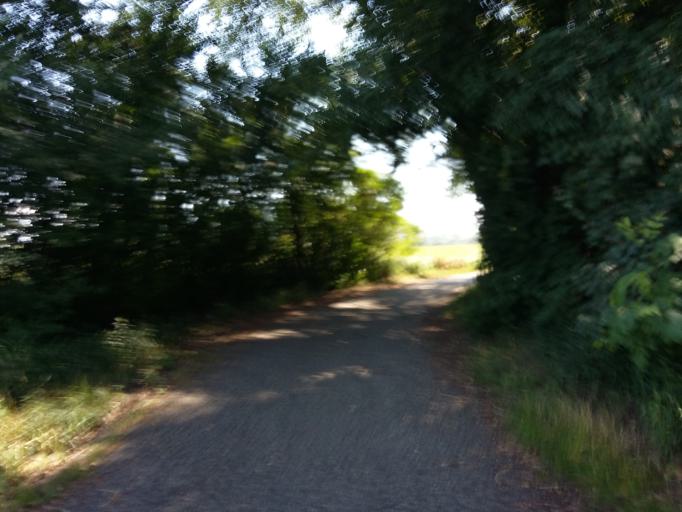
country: AT
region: Lower Austria
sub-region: Politischer Bezirk Bruck an der Leitha
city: Hainburg an der Donau
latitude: 48.2207
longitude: 16.9627
